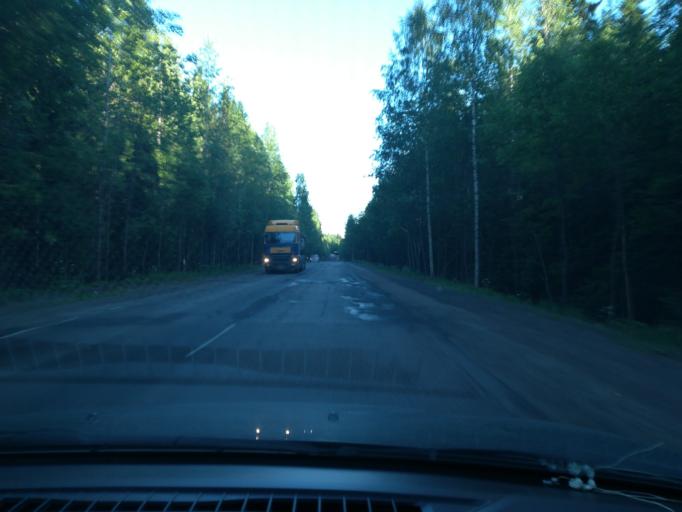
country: RU
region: Leningrad
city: Lesogorskiy
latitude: 60.9839
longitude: 28.9083
